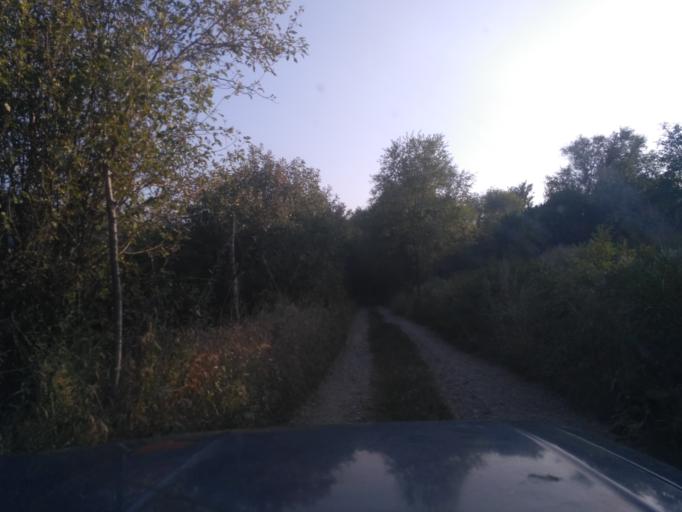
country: KZ
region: Almaty Oblysy
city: Burunday
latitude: 43.1544
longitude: 76.3715
